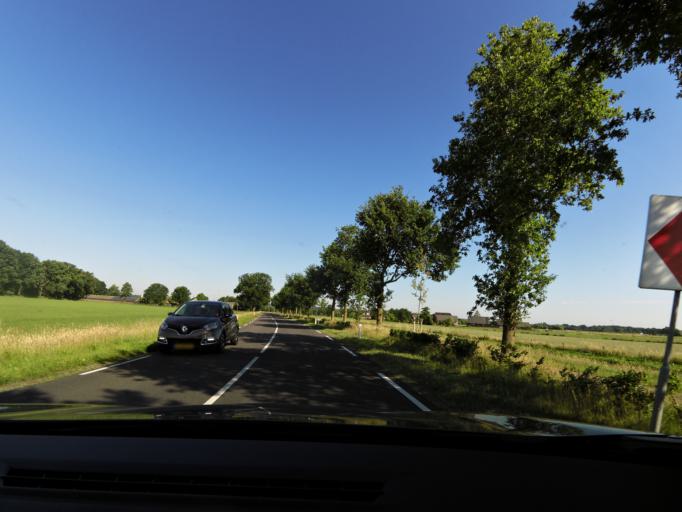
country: NL
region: Overijssel
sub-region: Gemeente Twenterand
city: Den Ham
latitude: 52.4417
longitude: 6.4331
